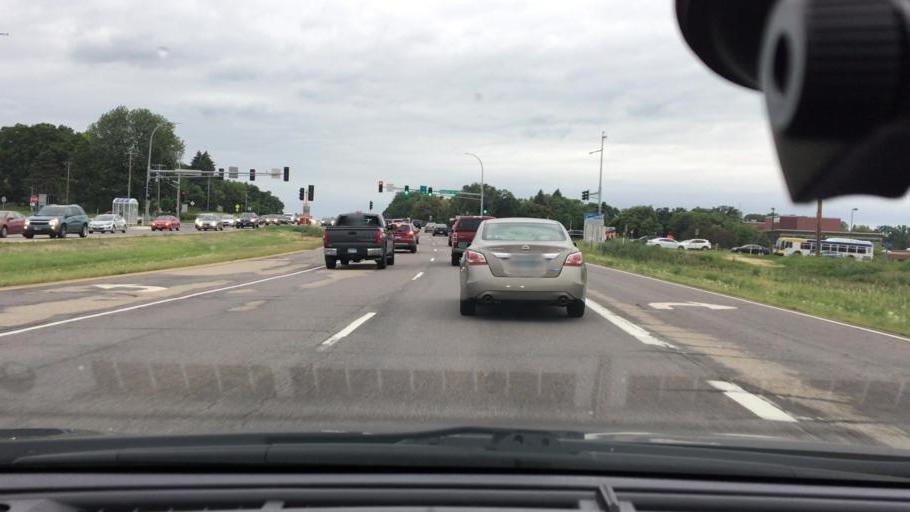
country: US
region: Minnesota
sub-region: Hennepin County
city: Golden Valley
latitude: 44.9848
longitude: -93.3589
